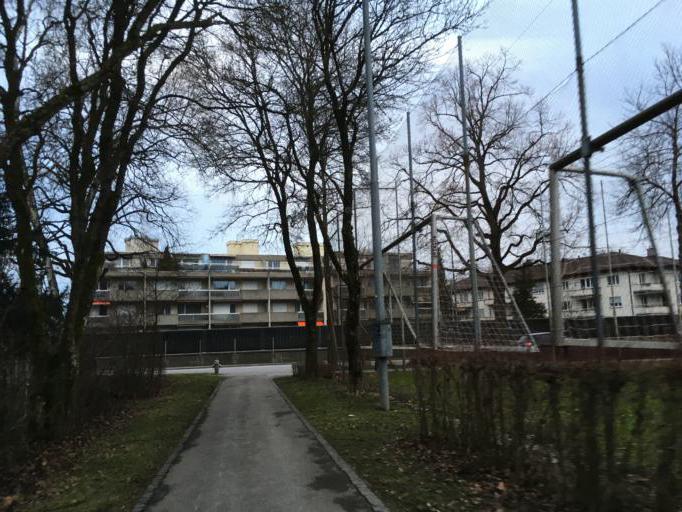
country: CH
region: Bern
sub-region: Bern-Mittelland District
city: Koniz
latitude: 46.9398
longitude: 7.4003
